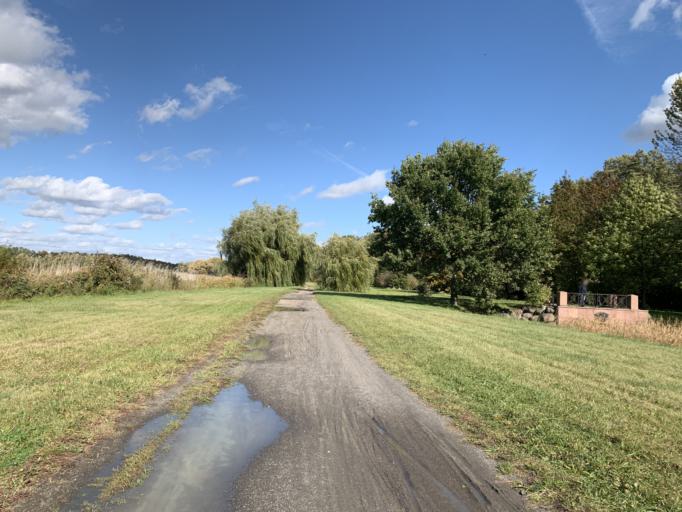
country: BY
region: Minsk
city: Nyasvizh
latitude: 53.2243
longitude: 26.6996
